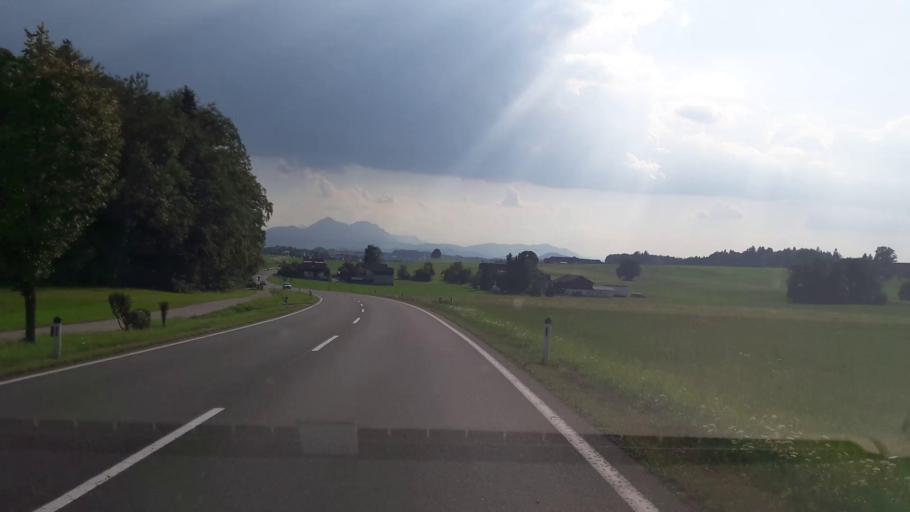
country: AT
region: Salzburg
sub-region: Politischer Bezirk Salzburg-Umgebung
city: Henndorf am Wallersee
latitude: 47.8801
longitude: 13.1676
